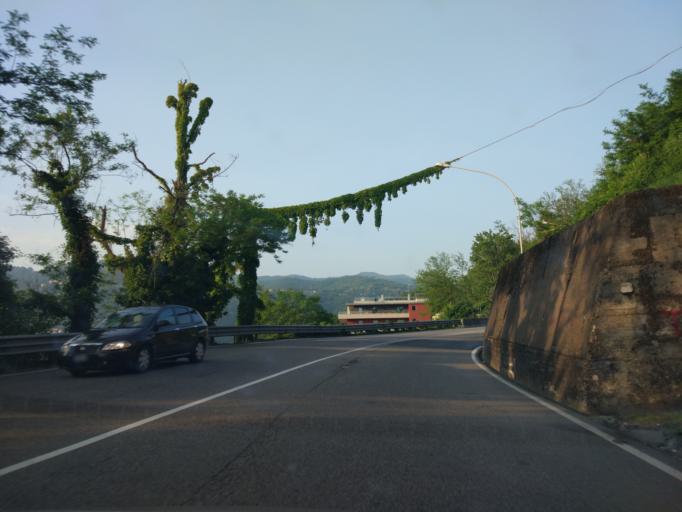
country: IT
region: Lombardy
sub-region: Provincia di Como
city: Como
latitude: 45.7913
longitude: 9.0974
